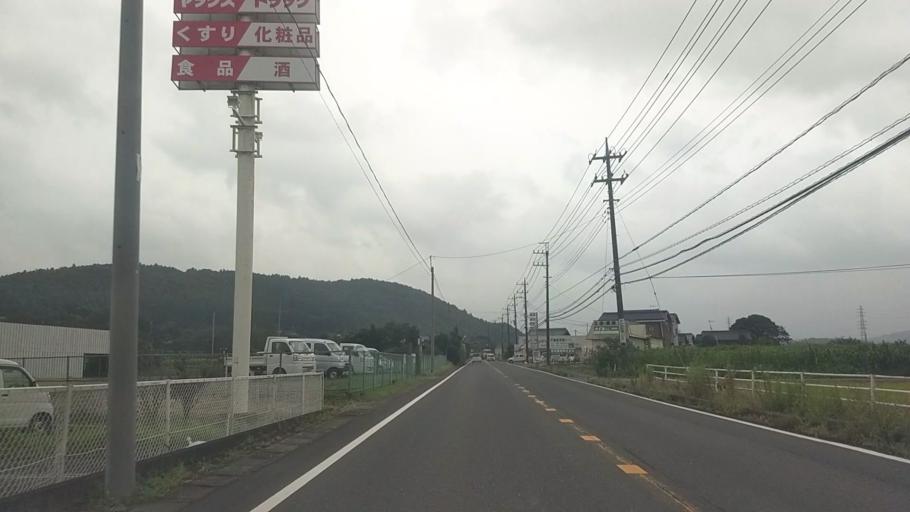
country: JP
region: Chiba
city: Kisarazu
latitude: 35.3087
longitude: 140.0666
